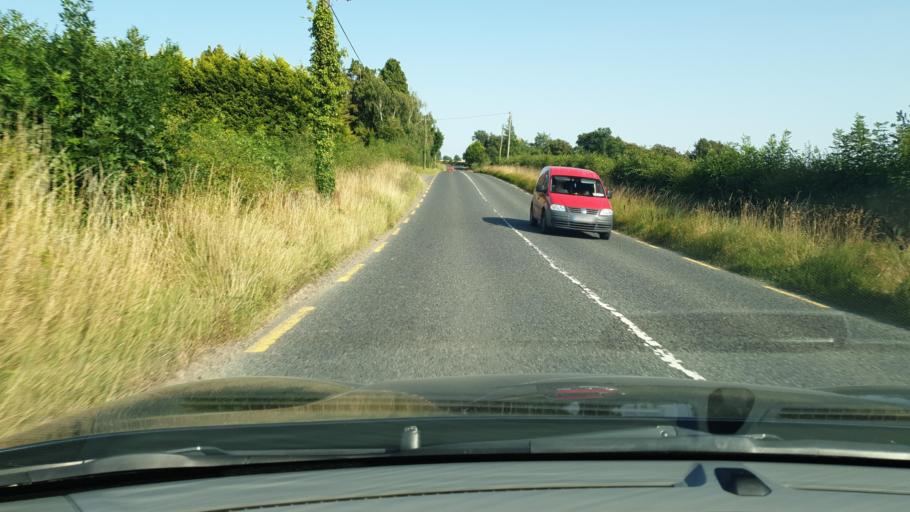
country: IE
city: Kentstown
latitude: 53.6356
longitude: -6.5940
